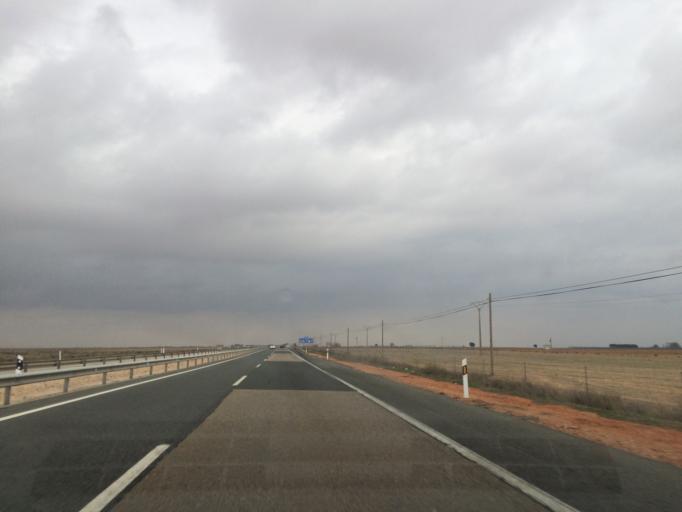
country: ES
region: Castille-La Mancha
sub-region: Province of Toledo
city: Tembleque
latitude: 39.6245
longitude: -3.5208
